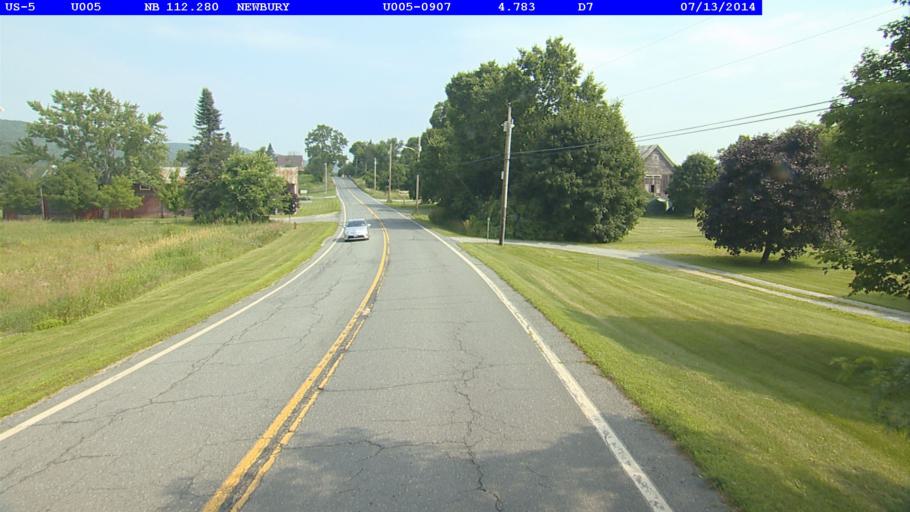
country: US
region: New Hampshire
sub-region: Grafton County
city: North Haverhill
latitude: 44.0911
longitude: -72.0473
